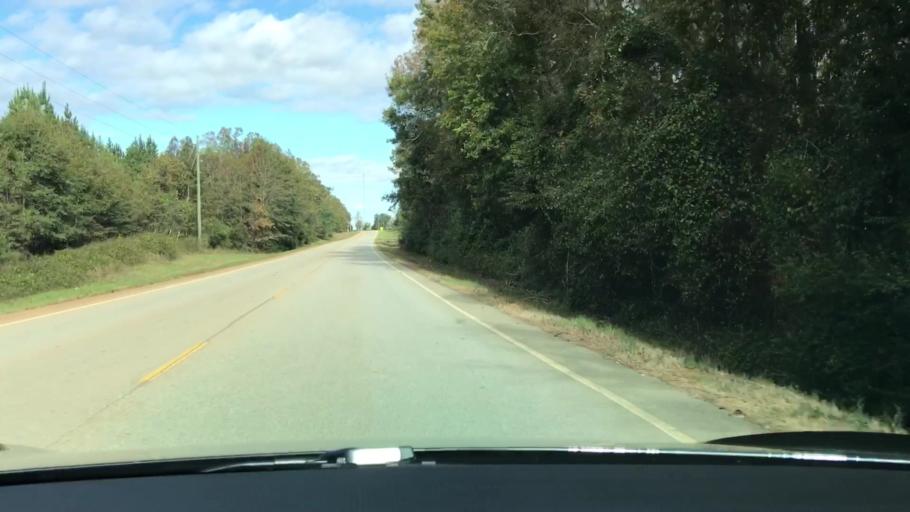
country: US
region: Georgia
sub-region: Jefferson County
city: Louisville
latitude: 33.0934
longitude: -82.4176
